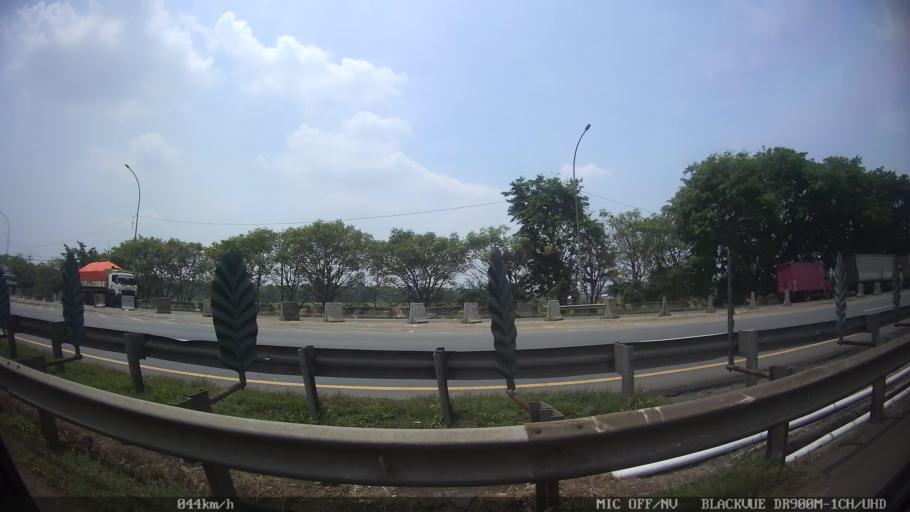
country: ID
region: West Java
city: Kresek
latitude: -6.1456
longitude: 106.2946
